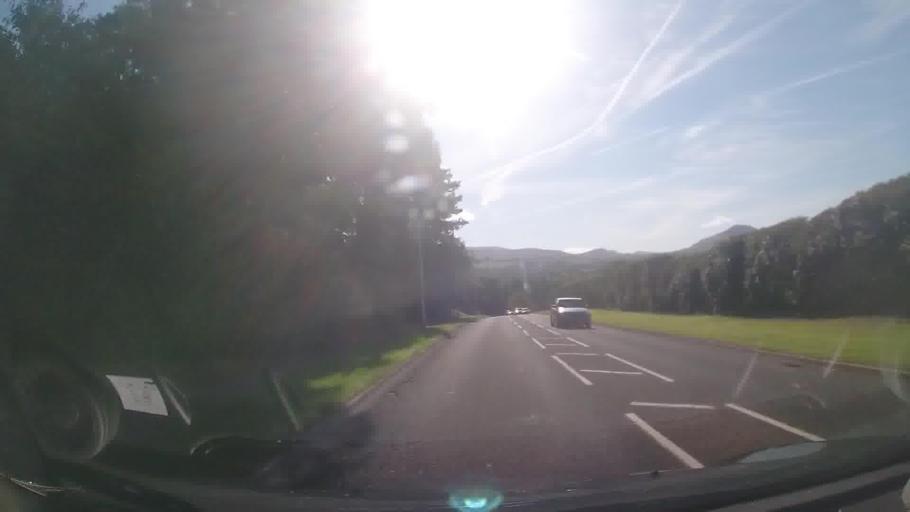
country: GB
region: Wales
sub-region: Sir Powys
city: Hay
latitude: 52.0037
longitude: -3.2421
